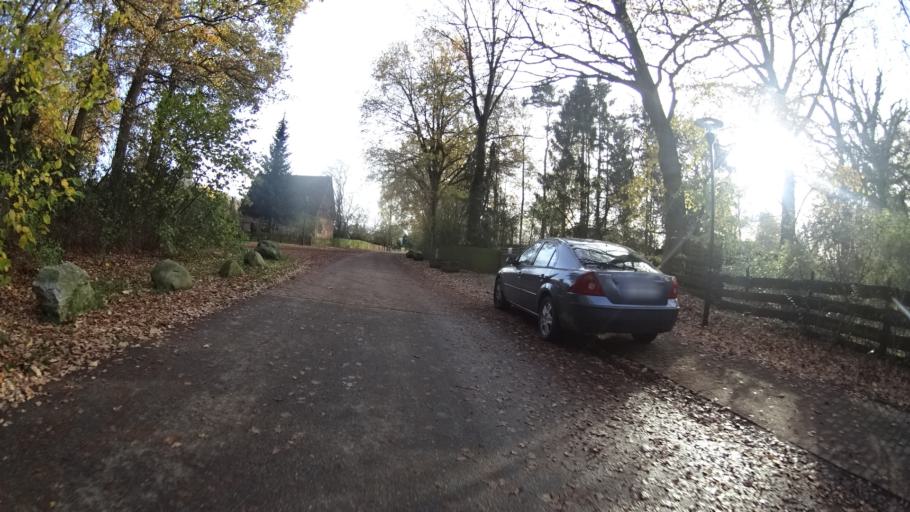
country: DE
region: Lower Saxony
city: Wendisch Evern
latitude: 53.2323
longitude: 10.4584
